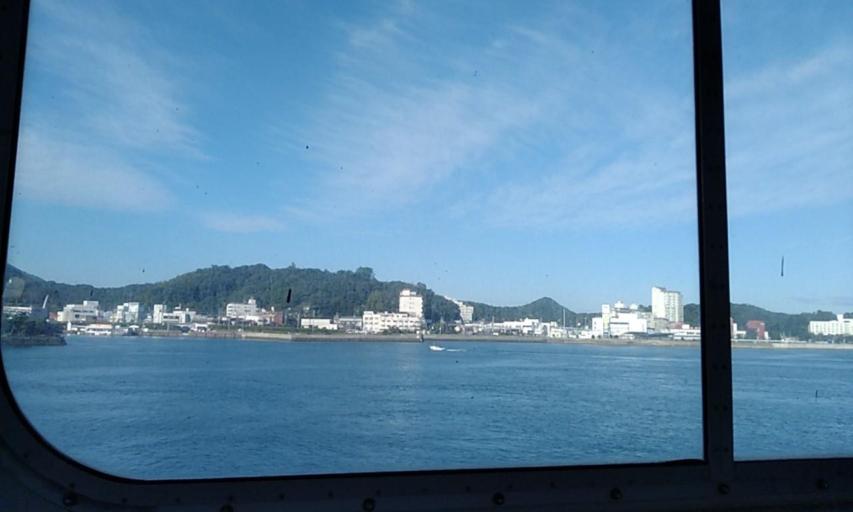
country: JP
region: Mie
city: Toba
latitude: 34.4849
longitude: 136.8492
